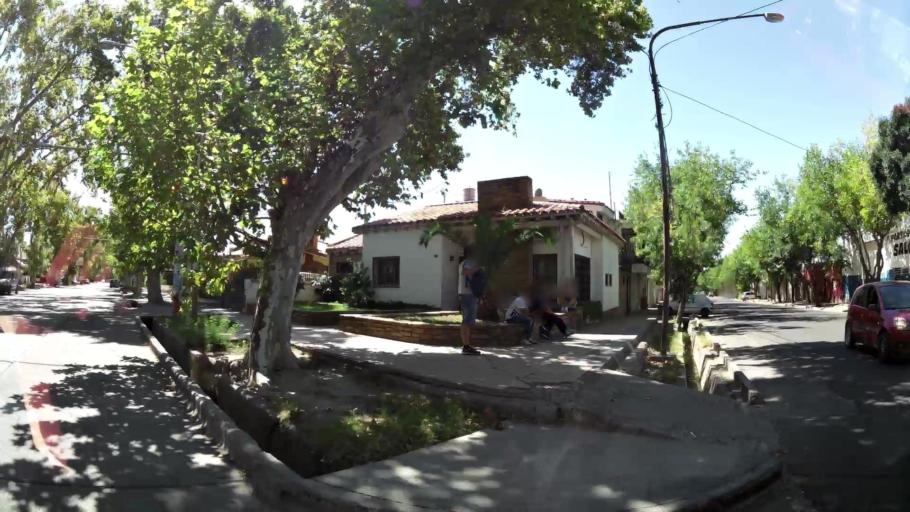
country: AR
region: Mendoza
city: Villa Nueva
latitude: -32.8995
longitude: -68.7942
